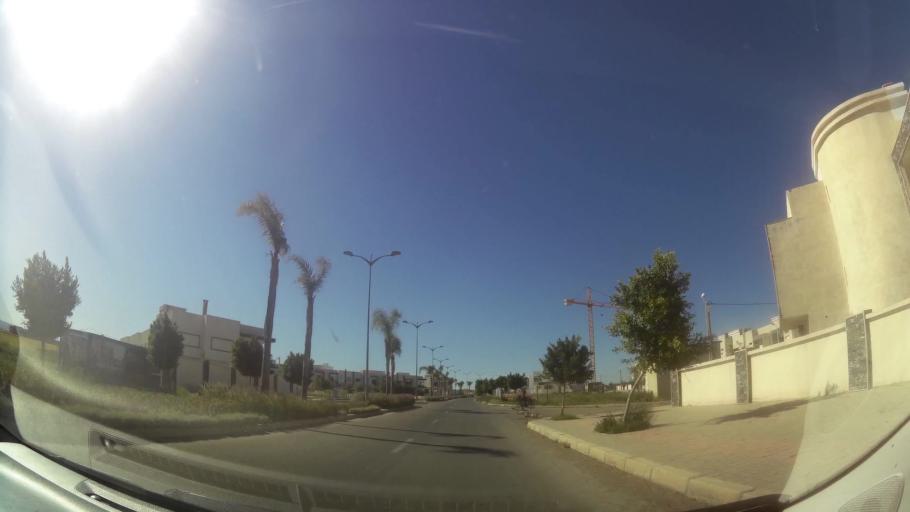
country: MA
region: Oriental
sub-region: Oujda-Angad
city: Oujda
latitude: 34.7326
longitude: -1.9179
